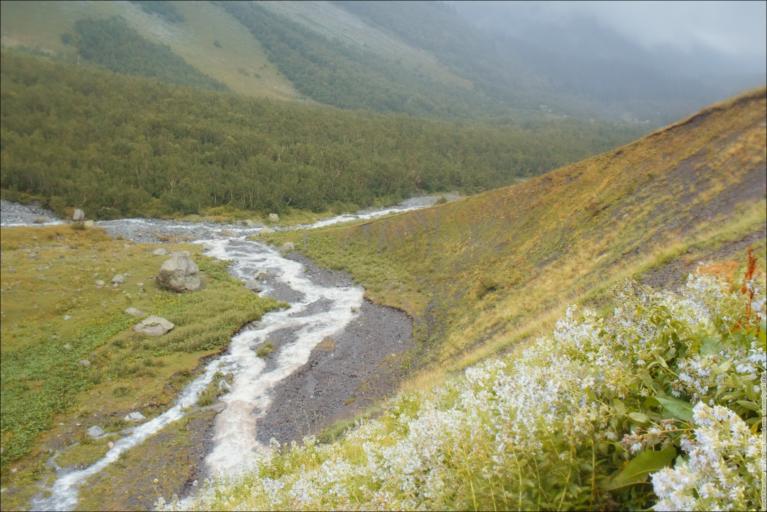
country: RU
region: Karachayevo-Cherkesiya
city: Nizhniy Arkhyz
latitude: 43.4420
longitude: 41.2857
